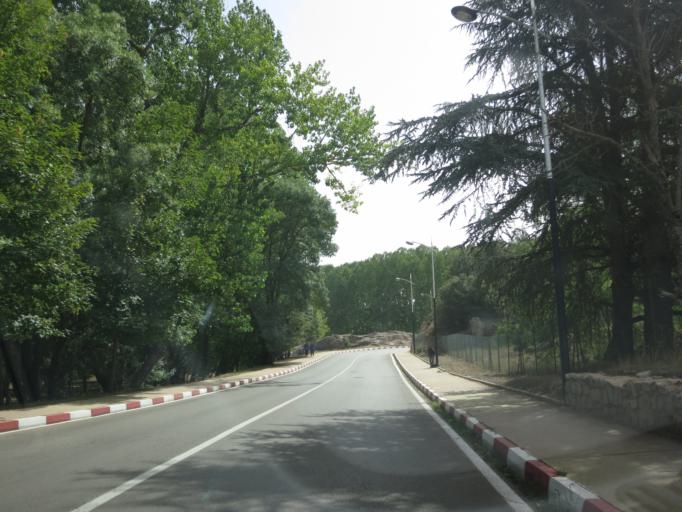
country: MA
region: Meknes-Tafilalet
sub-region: Ifrane
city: Ifrane
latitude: 33.5218
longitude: -5.0964
